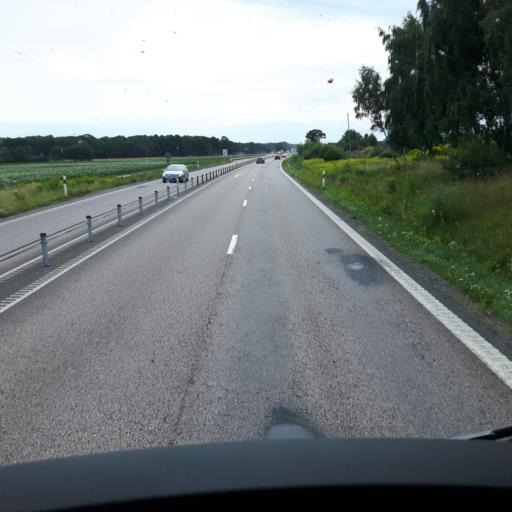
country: SE
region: Skane
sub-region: Hassleholms Kommun
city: Vinslov
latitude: 56.1150
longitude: 13.8550
